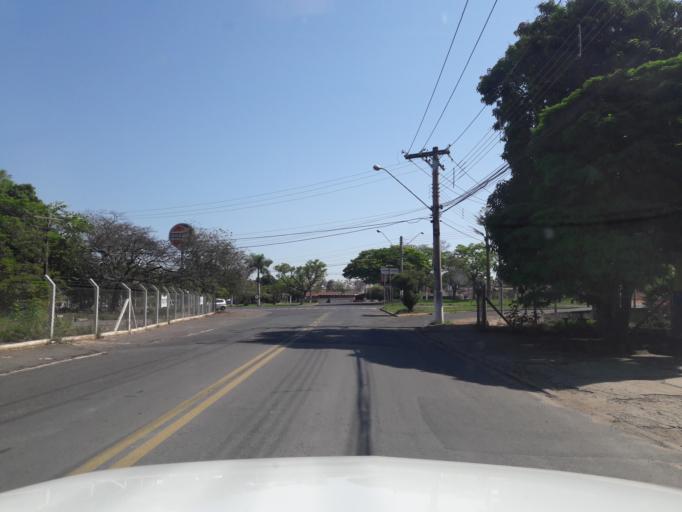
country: BR
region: Sao Paulo
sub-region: Moji-Guacu
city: Mogi-Gaucu
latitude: -22.3641
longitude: -46.9529
